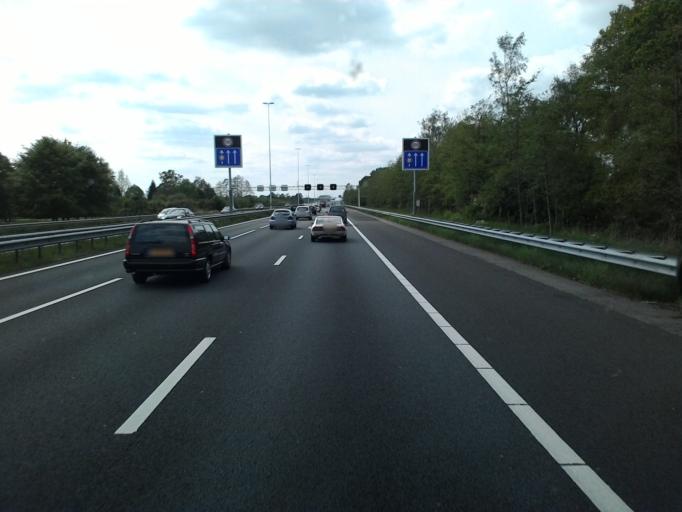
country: NL
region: Utrecht
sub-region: Gemeente Utrechtse Heuvelrug
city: Overberg
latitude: 52.0469
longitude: 5.5058
